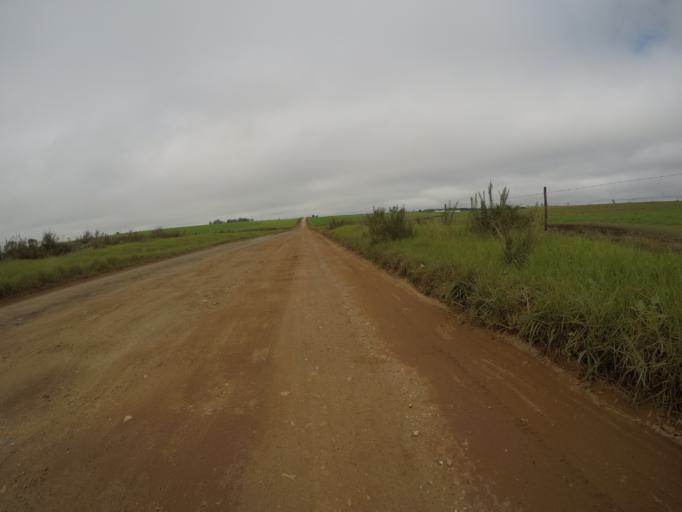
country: ZA
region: Eastern Cape
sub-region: Cacadu District Municipality
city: Kareedouw
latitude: -34.0247
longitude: 24.2412
